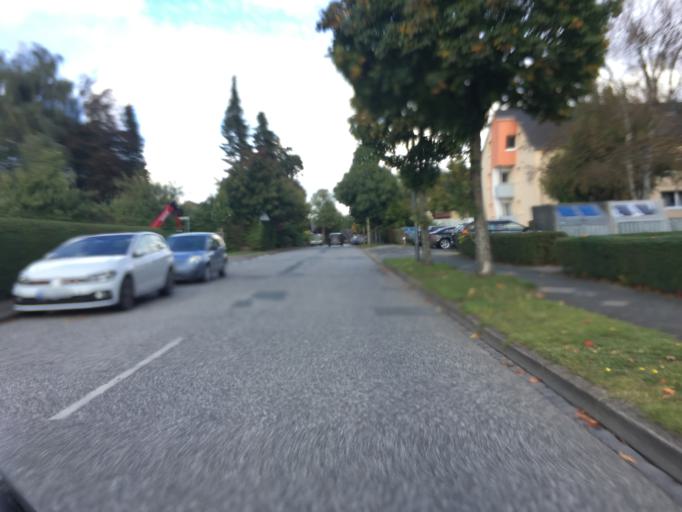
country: DE
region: Schleswig-Holstein
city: Heiligenstedten
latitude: 53.9412
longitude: 9.4942
